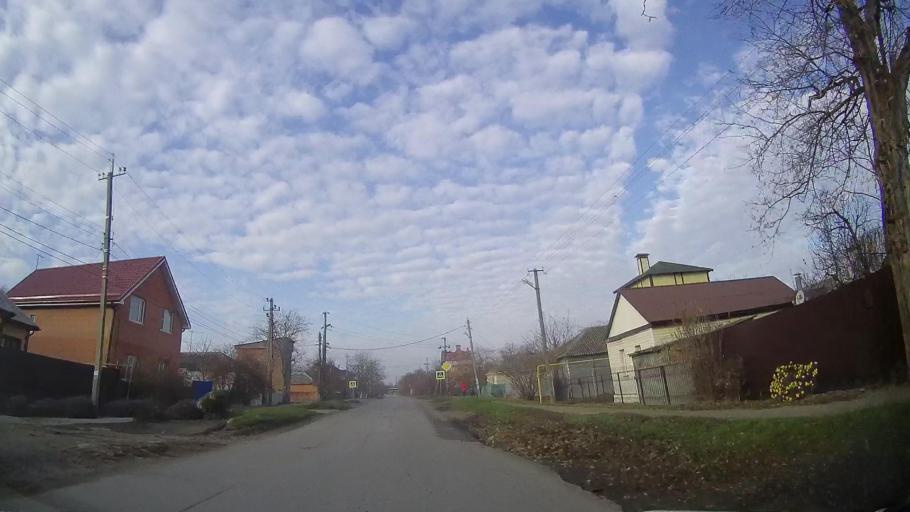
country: RU
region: Rostov
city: Bataysk
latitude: 47.1306
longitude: 39.7784
